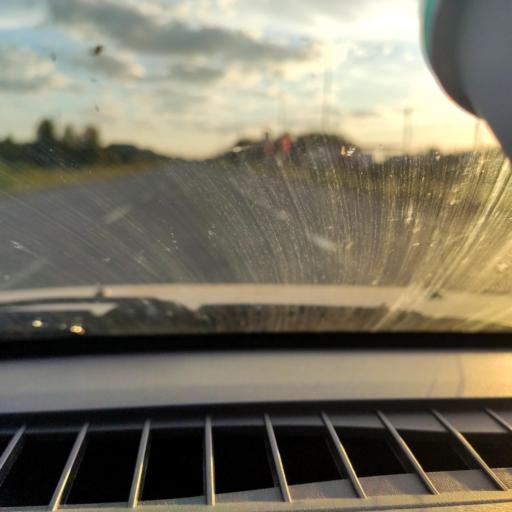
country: RU
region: Kirov
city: Kotel'nich
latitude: 58.3291
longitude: 48.2695
